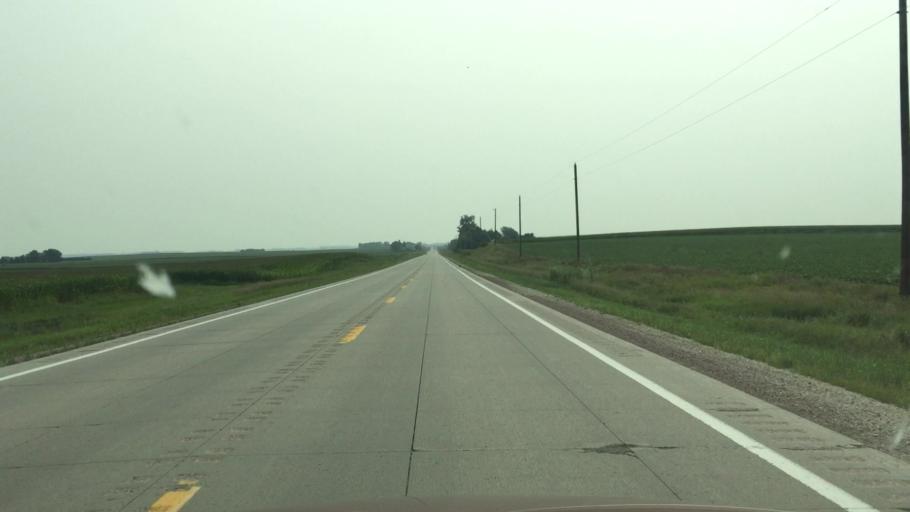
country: US
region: Iowa
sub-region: Osceola County
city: Sibley
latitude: 43.4327
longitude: -95.6562
